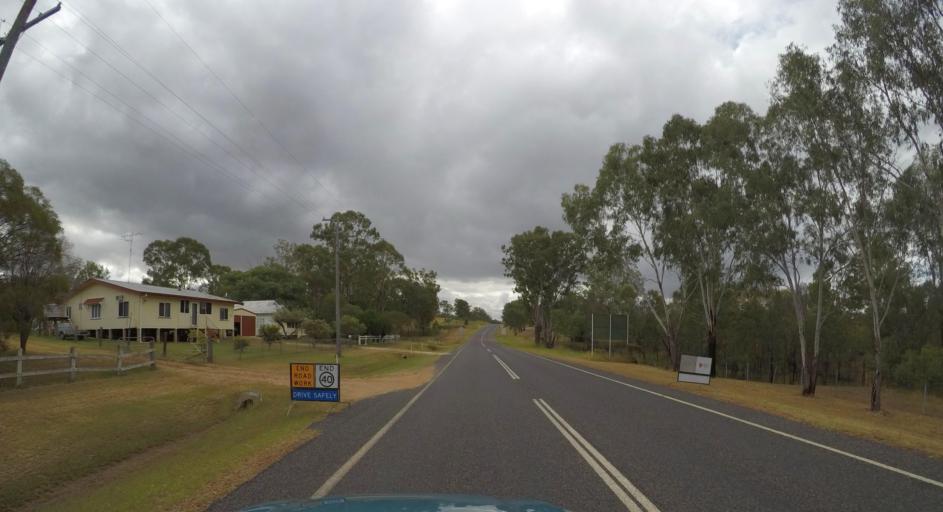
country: AU
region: Queensland
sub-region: North Burnett
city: Gayndah
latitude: -25.3646
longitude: 151.1205
